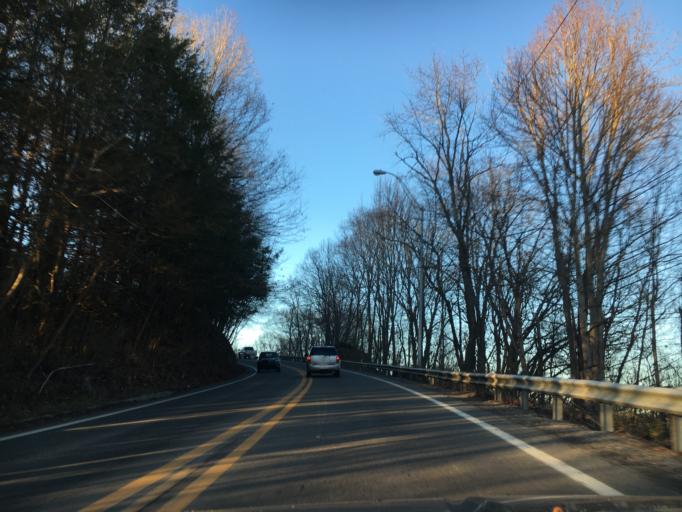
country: US
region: West Virginia
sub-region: Raleigh County
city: Beaver
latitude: 37.7649
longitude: -81.1567
